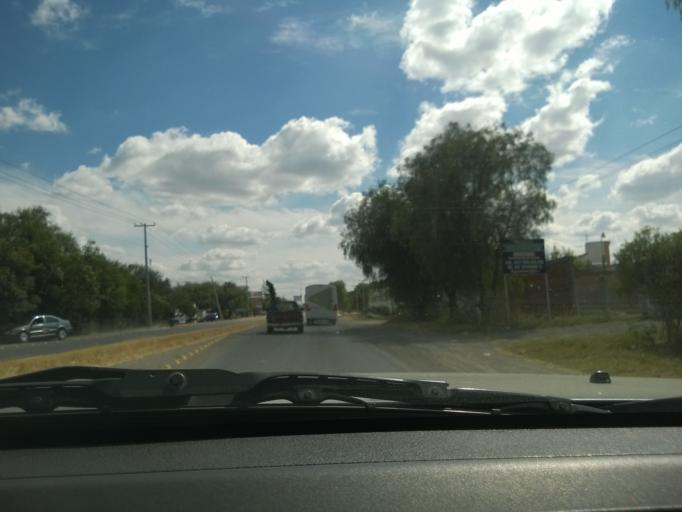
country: MX
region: Guanajuato
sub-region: Leon
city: El CERESO
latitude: 20.9905
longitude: -101.7026
